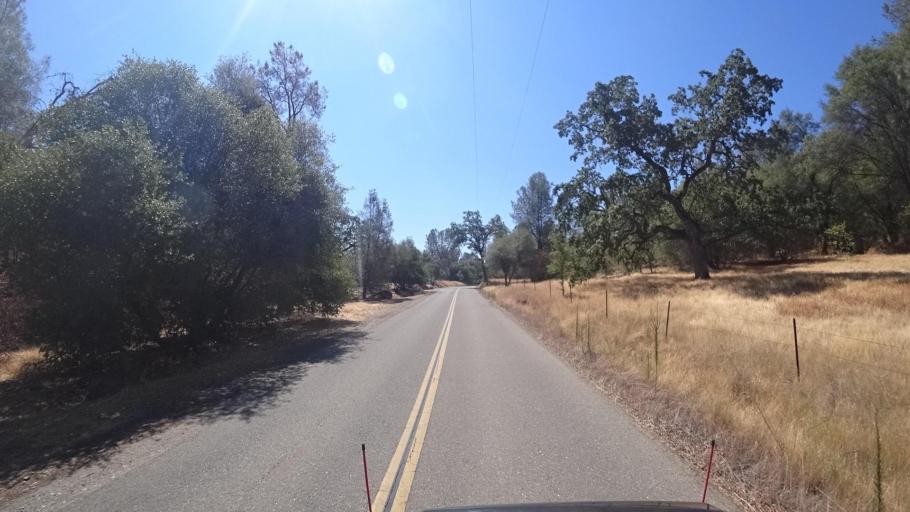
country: US
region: California
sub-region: Mariposa County
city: Mariposa
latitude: 37.4321
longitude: -119.9048
